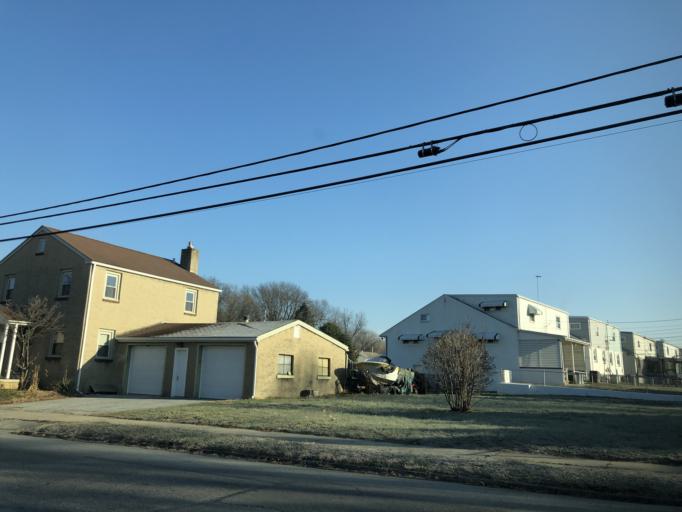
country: US
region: Pennsylvania
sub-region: Chester County
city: Downingtown
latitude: 40.0069
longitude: -75.6951
